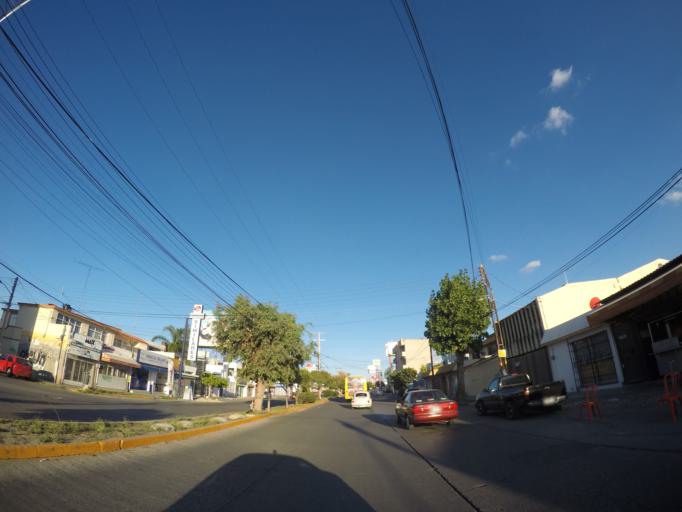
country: MX
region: San Luis Potosi
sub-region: San Luis Potosi
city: San Luis Potosi
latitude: 22.1360
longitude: -100.9819
